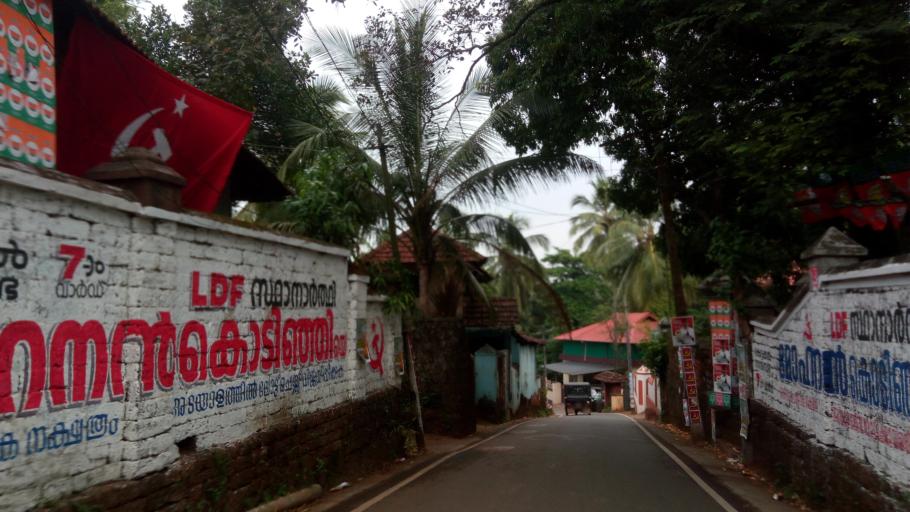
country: IN
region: Kerala
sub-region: Malappuram
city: Malappuram
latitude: 10.9922
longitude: 76.0084
